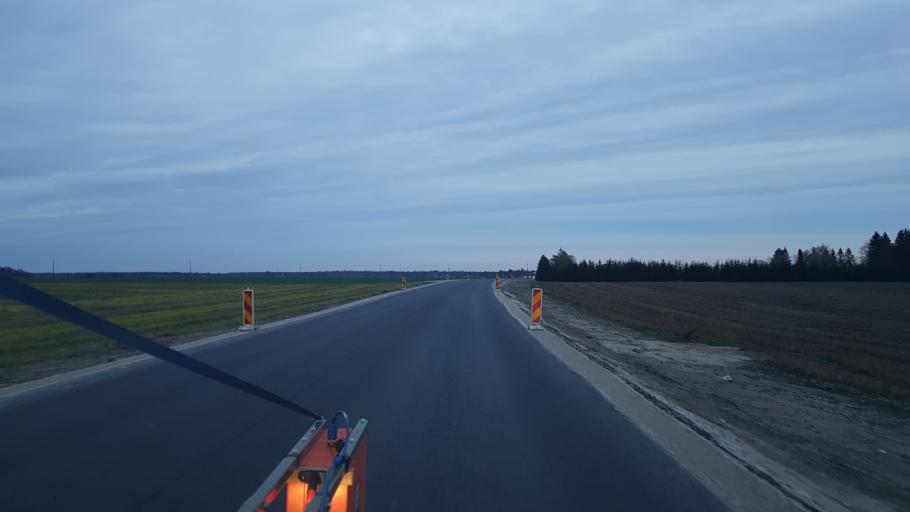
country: EE
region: Jogevamaa
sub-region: Jogeva linn
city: Jogeva
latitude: 58.7320
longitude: 26.2080
